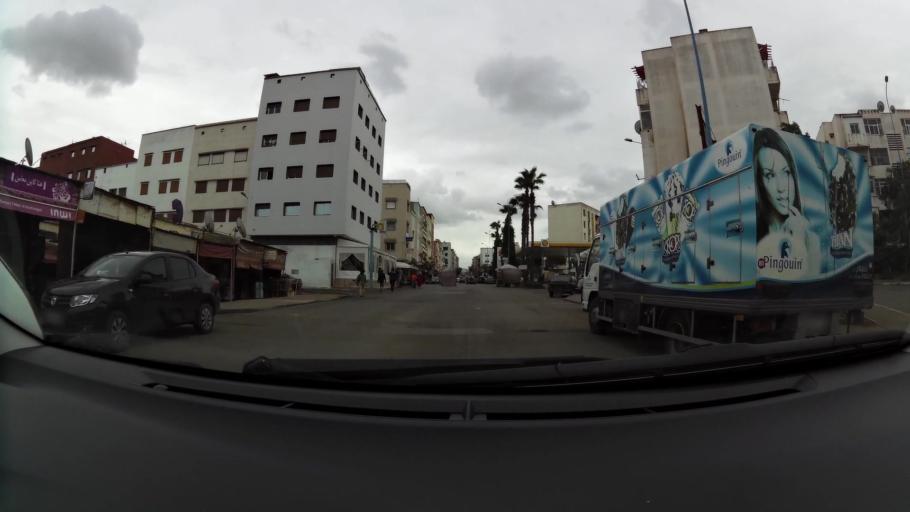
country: MA
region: Grand Casablanca
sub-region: Casablanca
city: Casablanca
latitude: 33.5745
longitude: -7.5546
